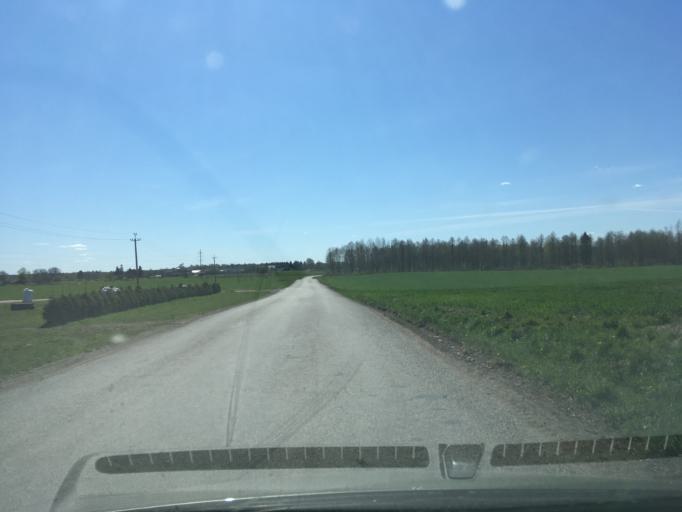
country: EE
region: Harju
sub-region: Raasiku vald
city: Arukula
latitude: 59.3890
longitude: 25.0804
